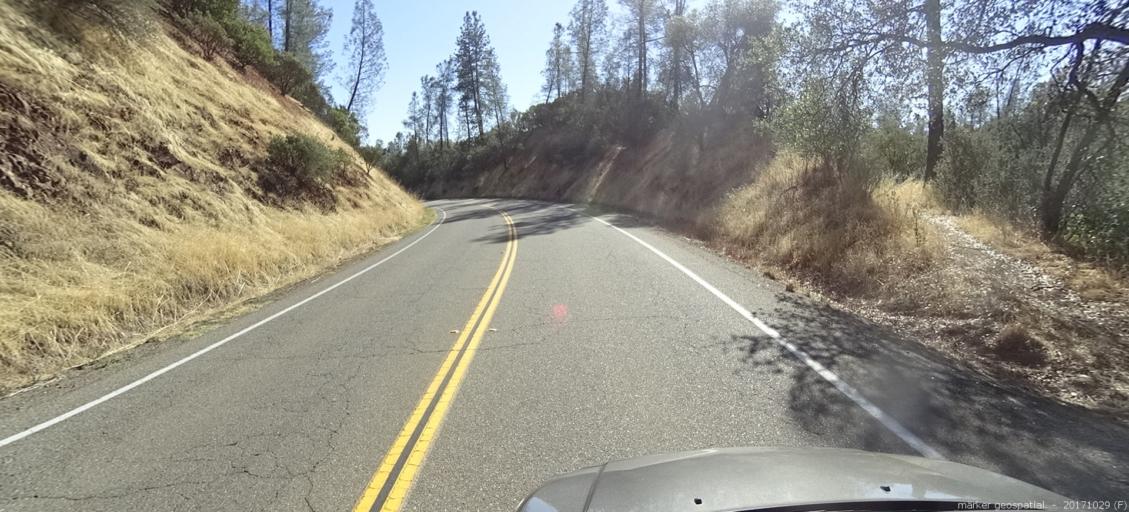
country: US
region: California
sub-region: Shasta County
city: Shasta
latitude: 40.4949
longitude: -122.4732
